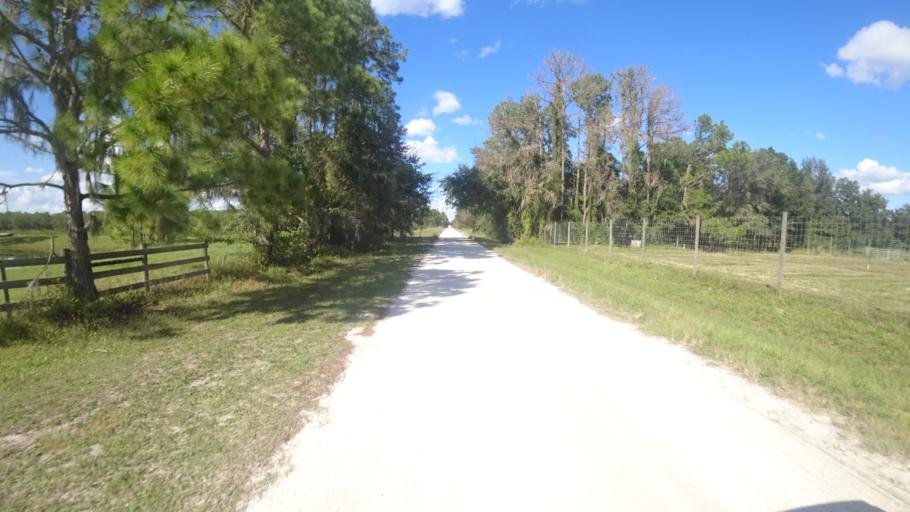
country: US
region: Florida
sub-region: Hardee County
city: Wauchula
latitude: 27.4745
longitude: -82.0555
